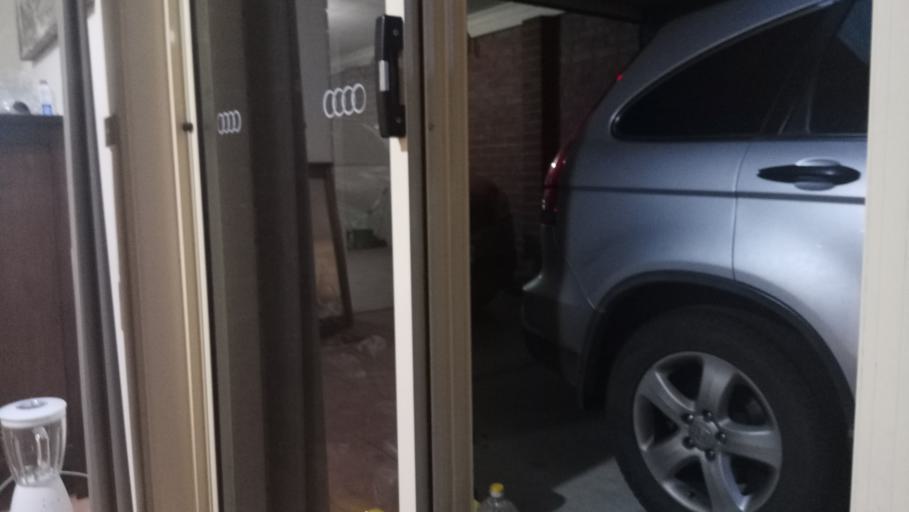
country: AU
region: Victoria
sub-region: Wyndham
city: Werribee
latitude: -37.8884
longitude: 144.6395
